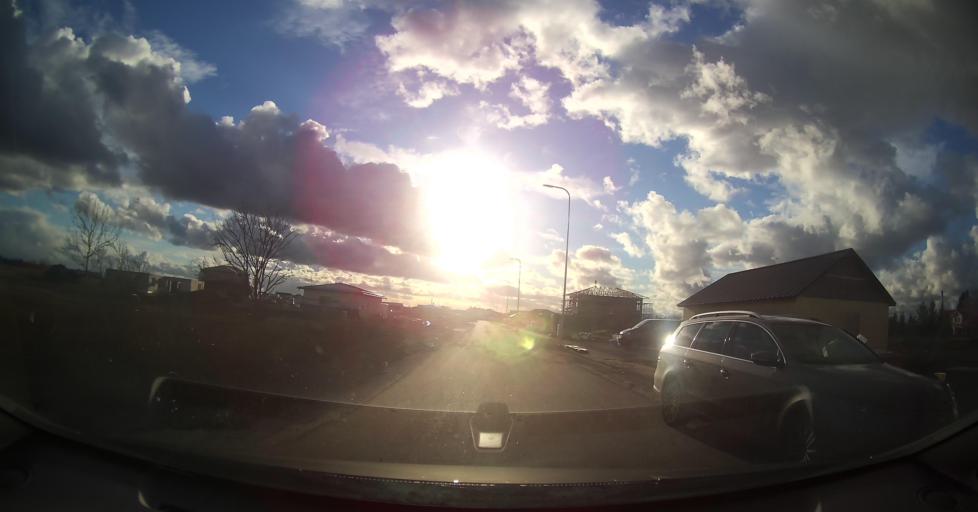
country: EE
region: Harju
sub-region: Joelaehtme vald
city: Loo
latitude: 59.4448
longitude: 24.9677
